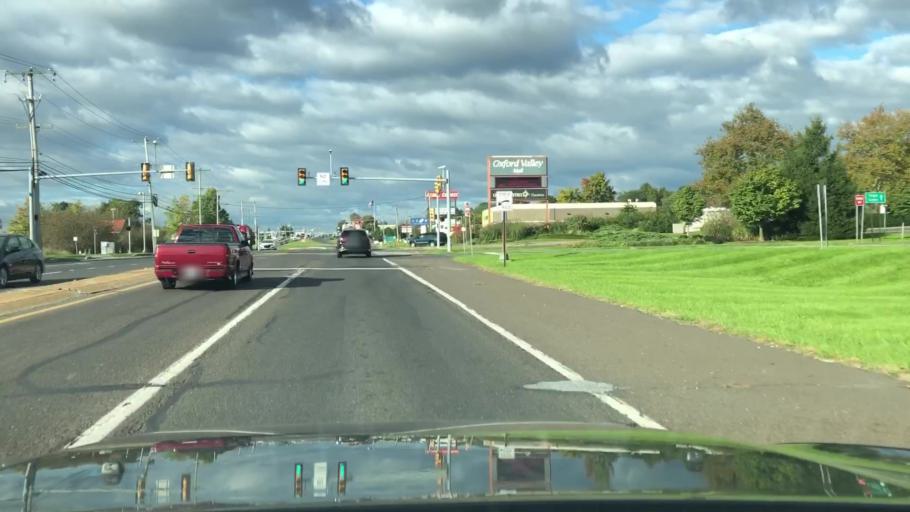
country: US
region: Pennsylvania
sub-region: Bucks County
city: Woodbourne
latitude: 40.1796
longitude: -74.8767
